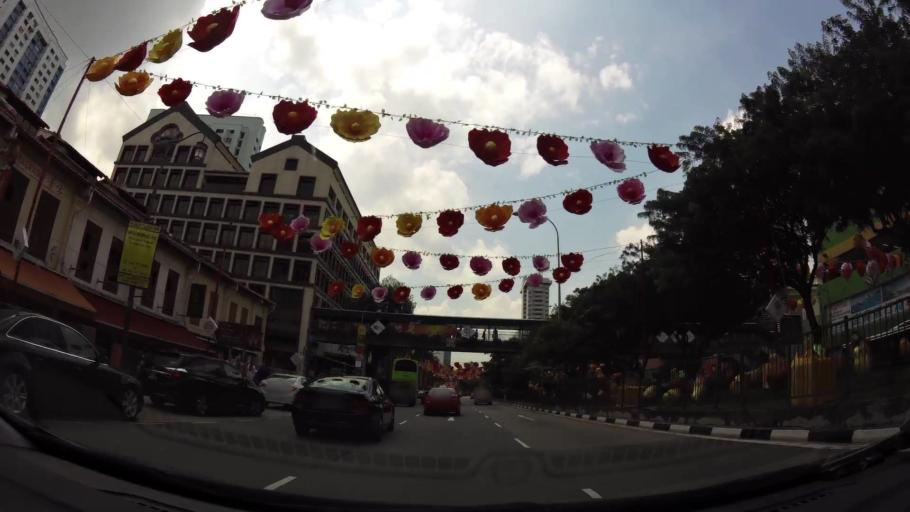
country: SG
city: Singapore
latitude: 1.2834
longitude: 103.8429
